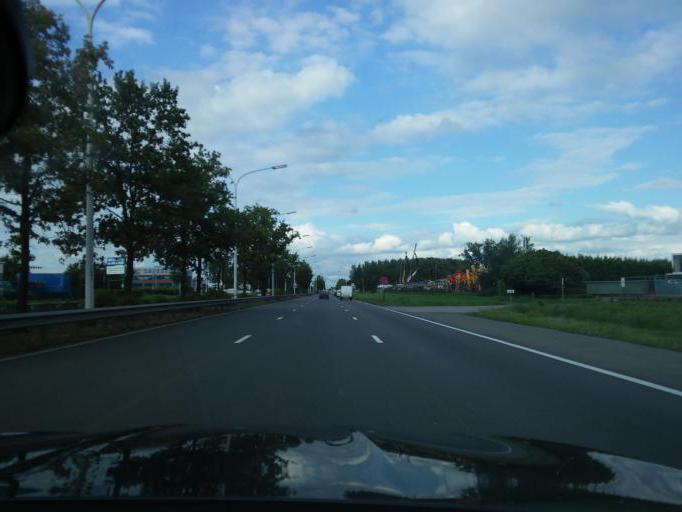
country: BE
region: Flanders
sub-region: Provincie Vlaams-Brabant
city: Londerzeel
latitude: 51.0336
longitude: 4.3265
